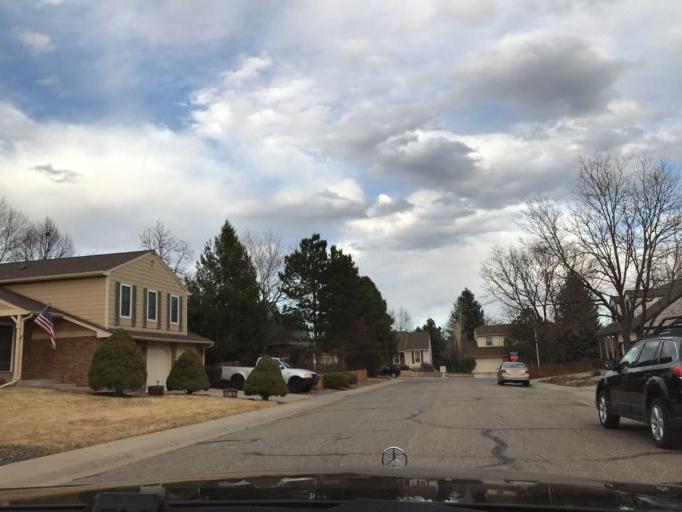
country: US
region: Colorado
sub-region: Jefferson County
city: Applewood
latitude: 39.8252
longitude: -105.1603
